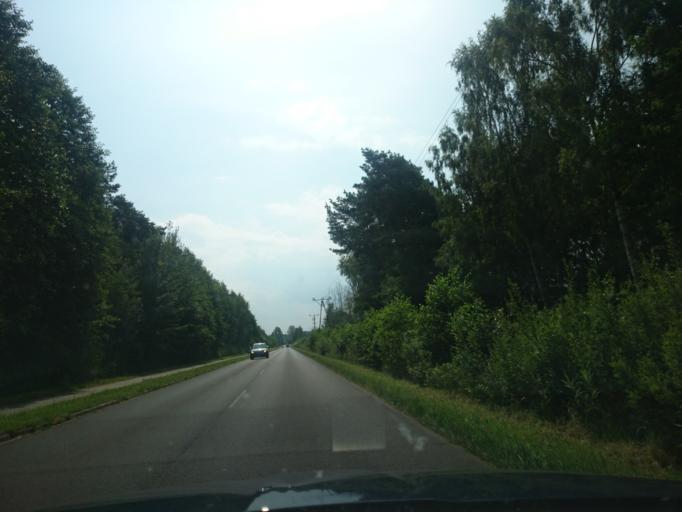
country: PL
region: West Pomeranian Voivodeship
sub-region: Powiat kamienski
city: Dziwnow
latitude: 53.9980
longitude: 14.6791
